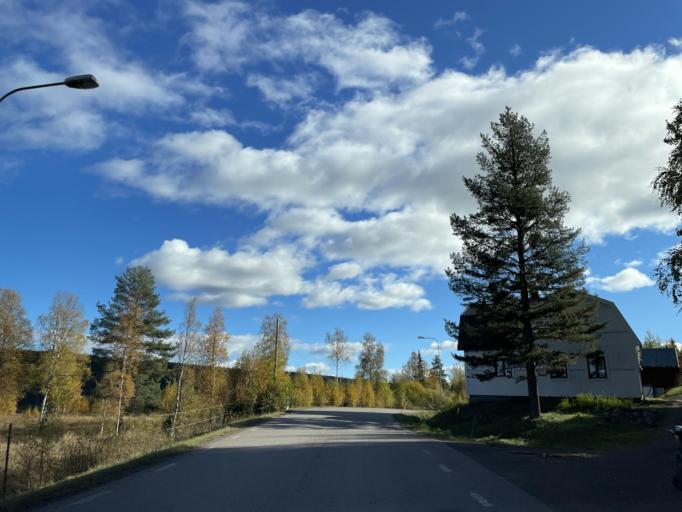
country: SE
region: Dalarna
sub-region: Malung-Saelens kommun
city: Malung
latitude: 61.1526
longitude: 13.2596
